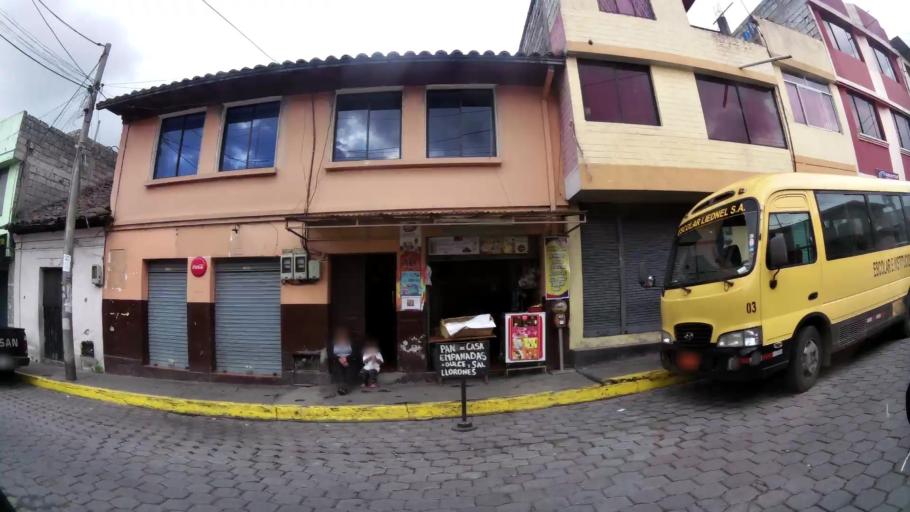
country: EC
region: Pichincha
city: Sangolqui
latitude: -0.3371
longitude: -78.4525
